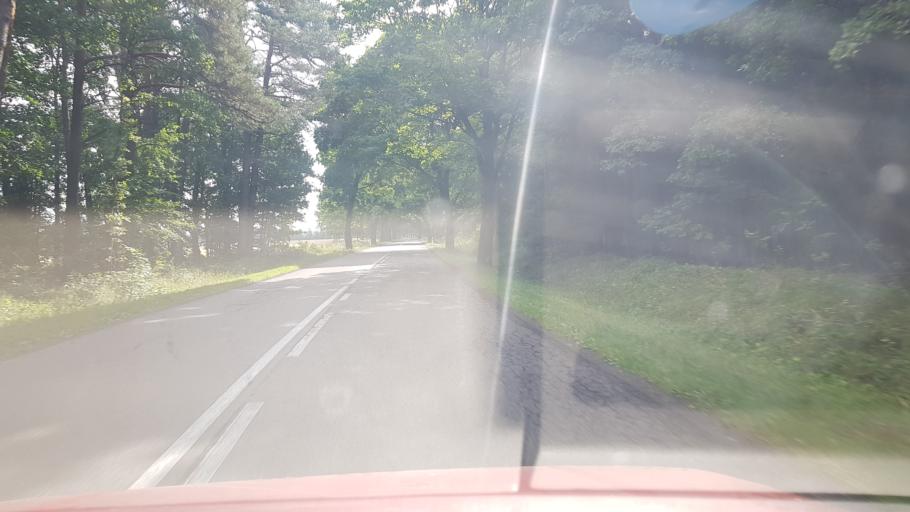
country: PL
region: West Pomeranian Voivodeship
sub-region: Powiat koszalinski
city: Polanow
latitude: 54.1137
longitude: 16.7769
